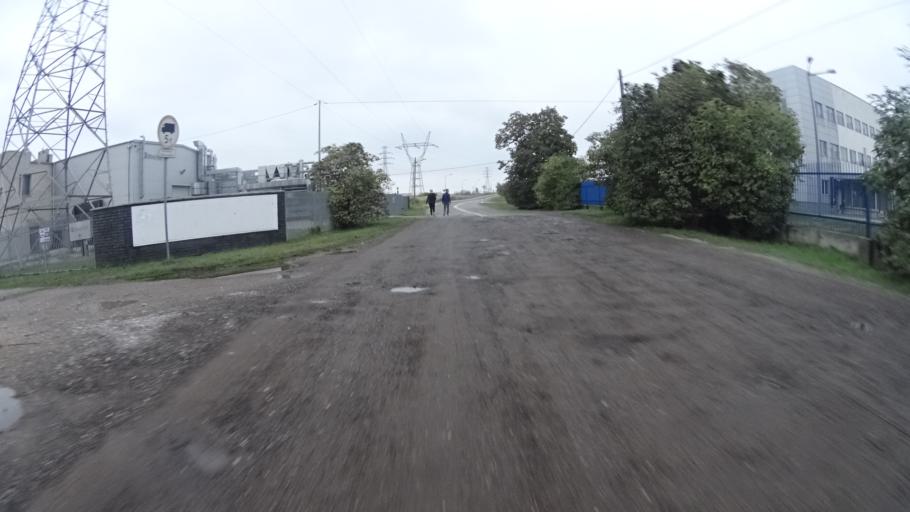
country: PL
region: Masovian Voivodeship
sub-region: Powiat warszawski zachodni
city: Babice
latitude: 52.2245
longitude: 20.8668
